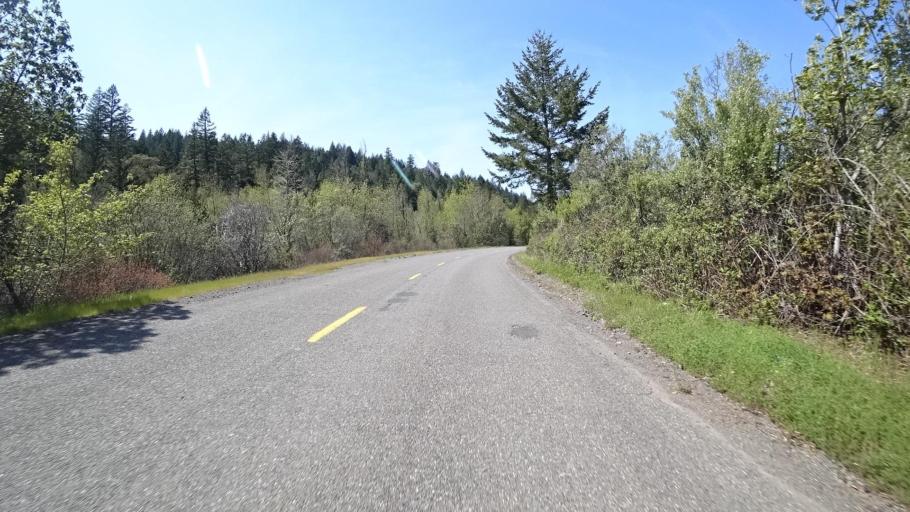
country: US
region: California
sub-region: Humboldt County
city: Redway
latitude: 40.3190
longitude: -123.6615
